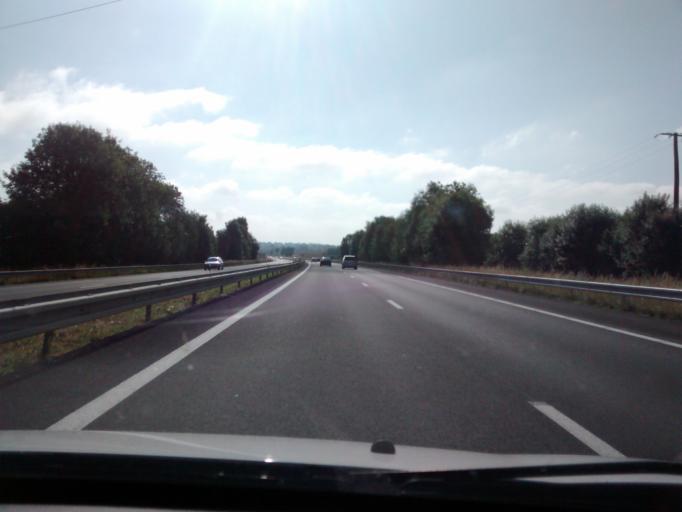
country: FR
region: Pays de la Loire
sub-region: Departement de la Mayenne
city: Vaiges
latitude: 48.0507
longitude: -0.4562
